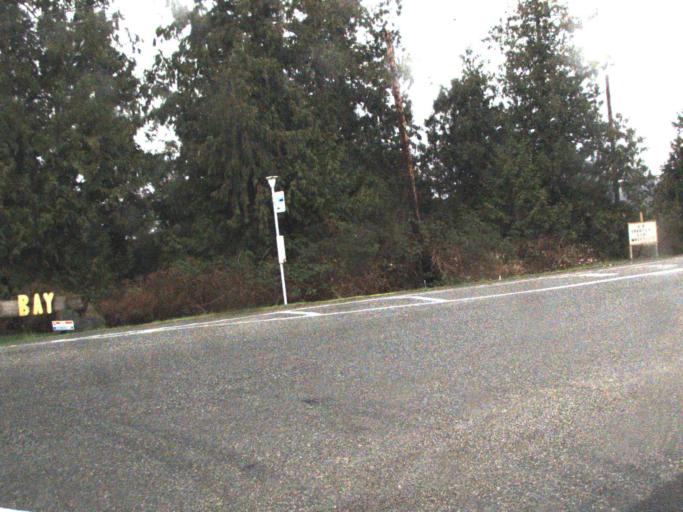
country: US
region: Washington
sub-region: Snohomish County
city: Stanwood
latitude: 48.2399
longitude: -122.4339
